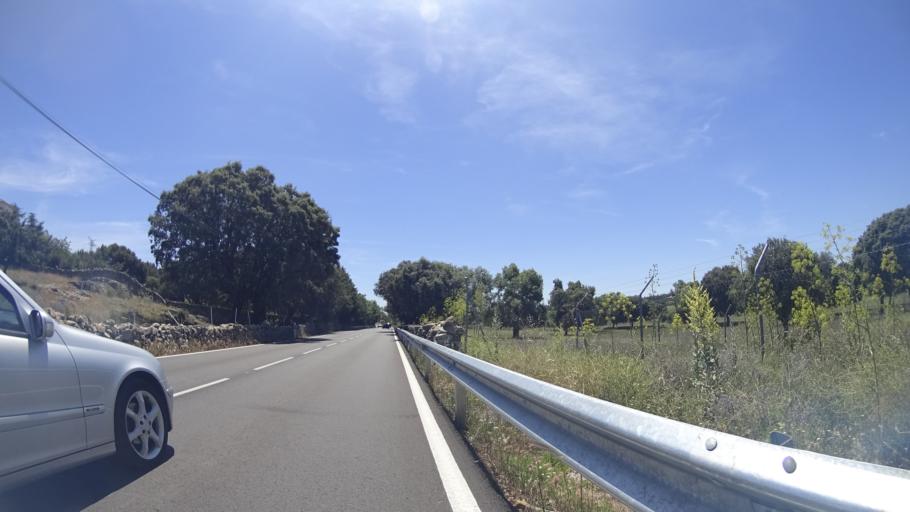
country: ES
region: Madrid
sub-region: Provincia de Madrid
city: Galapagar
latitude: 40.5944
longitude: -4.0139
